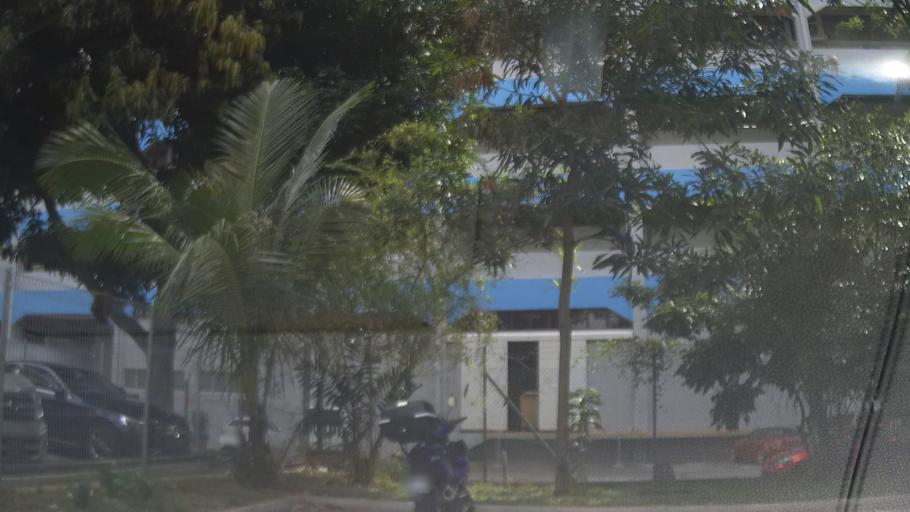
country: SG
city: Singapore
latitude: 1.3177
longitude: 103.8768
